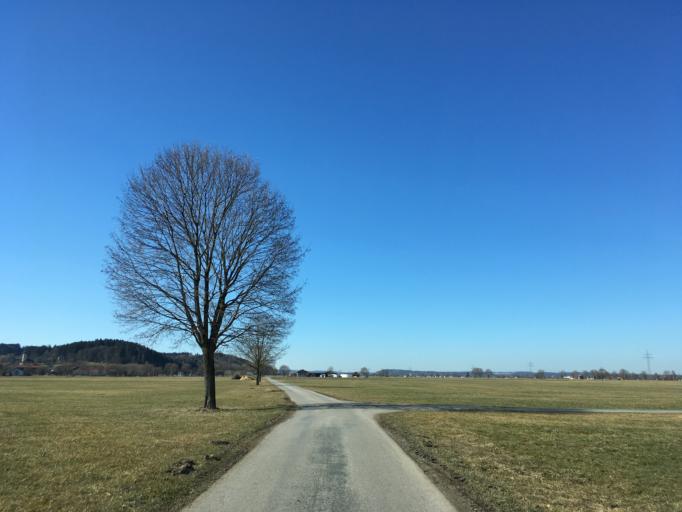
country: DE
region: Bavaria
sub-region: Upper Bavaria
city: Bad Aibling
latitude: 47.8438
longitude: 11.9872
